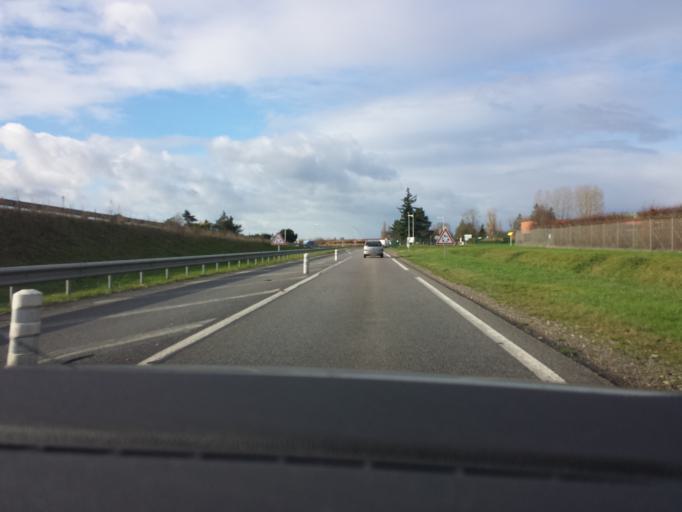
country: FR
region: Haute-Normandie
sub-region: Departement de l'Eure
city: Gravigny
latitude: 49.0152
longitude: 1.1971
